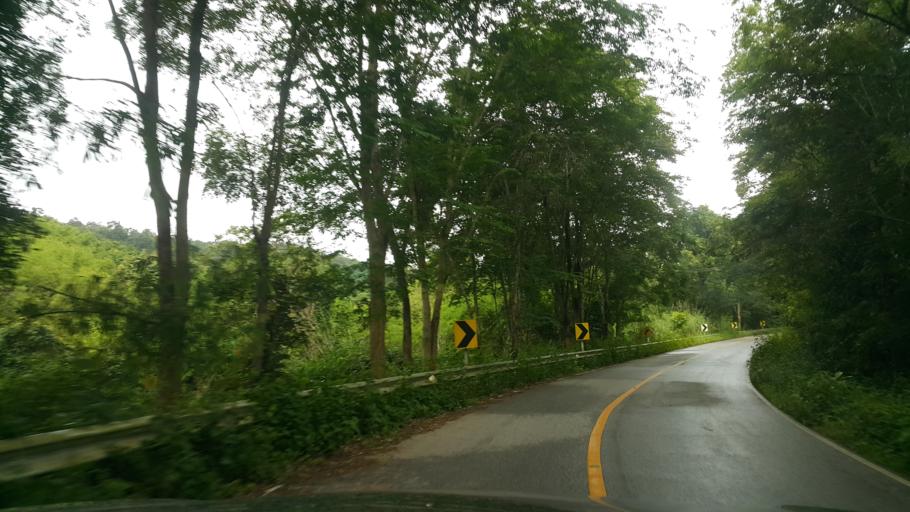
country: TH
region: Loei
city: Na Haeo
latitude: 17.4864
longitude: 100.8052
